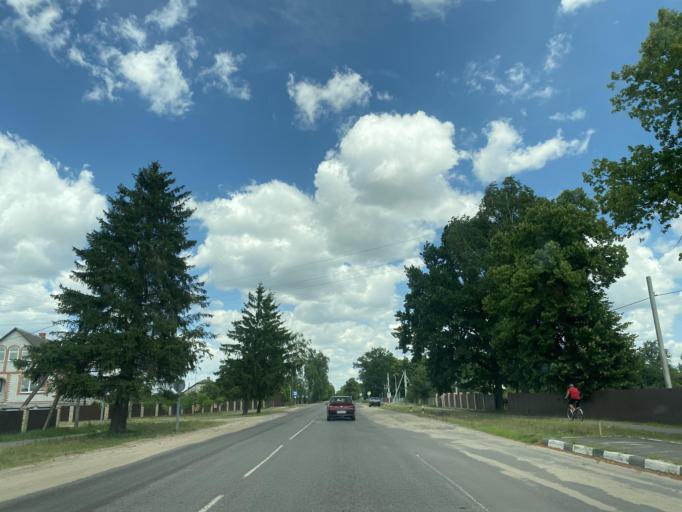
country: BY
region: Brest
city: Ivanava
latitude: 52.1598
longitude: 25.5459
